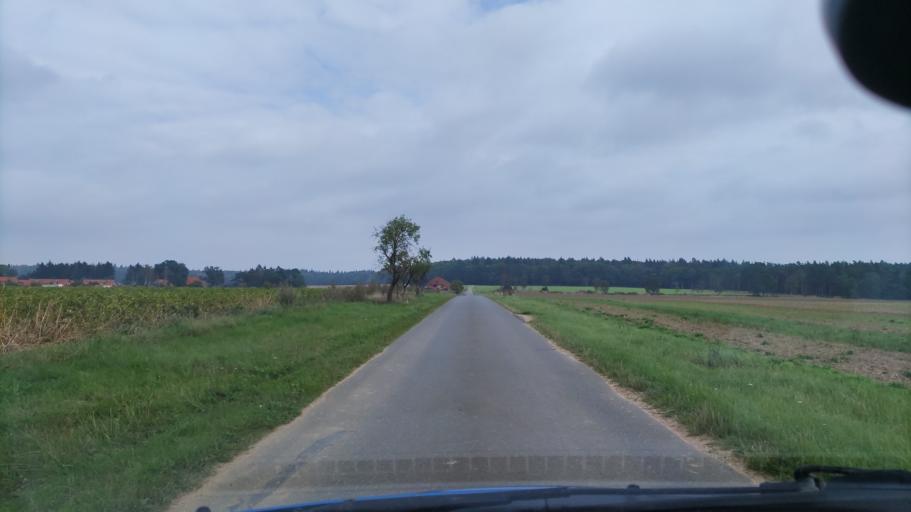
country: DE
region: Lower Saxony
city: Altenmedingen
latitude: 53.1549
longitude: 10.5674
